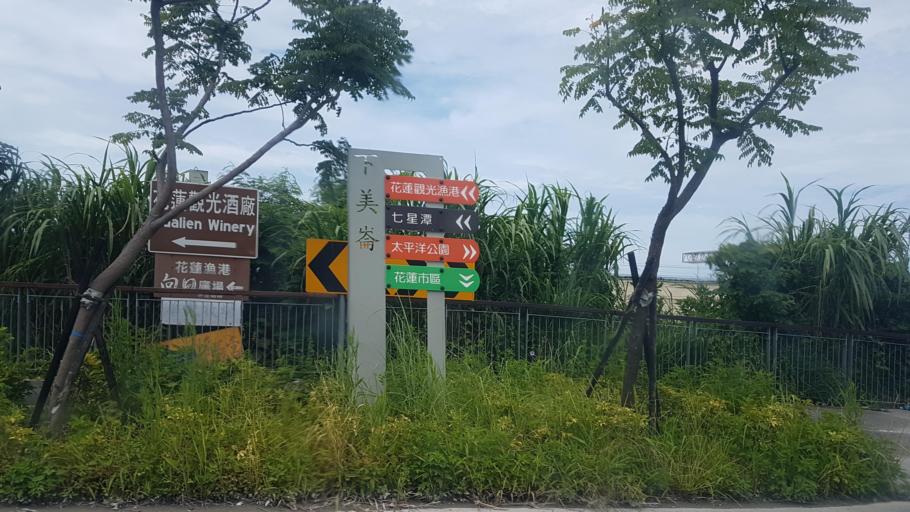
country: TW
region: Taiwan
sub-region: Hualien
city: Hualian
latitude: 24.0015
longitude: 121.6346
